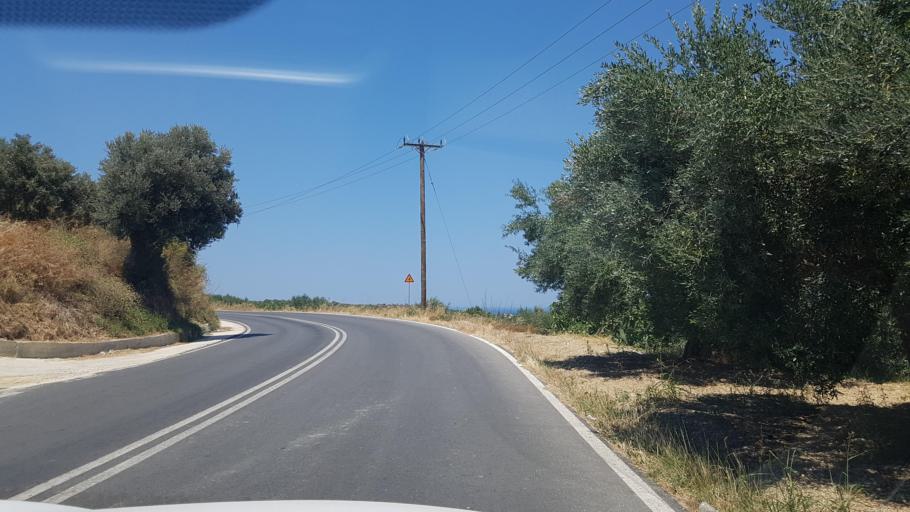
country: GR
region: Crete
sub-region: Nomos Rethymnis
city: Rethymno
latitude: 35.3560
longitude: 24.5842
